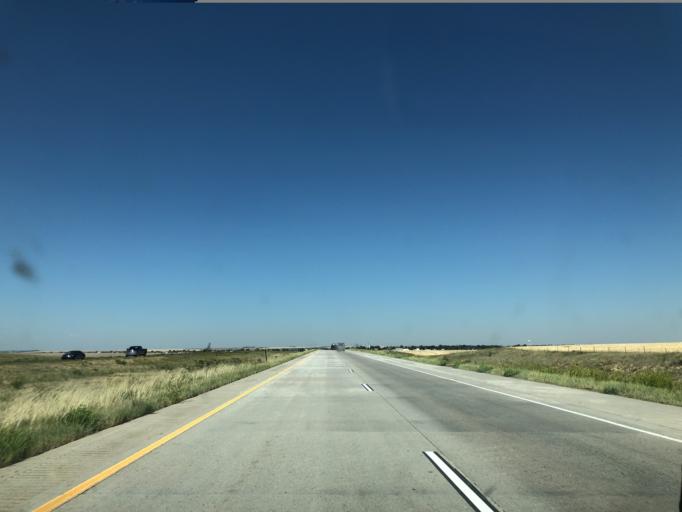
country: US
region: Colorado
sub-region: Adams County
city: Strasburg
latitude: 39.7306
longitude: -104.2962
